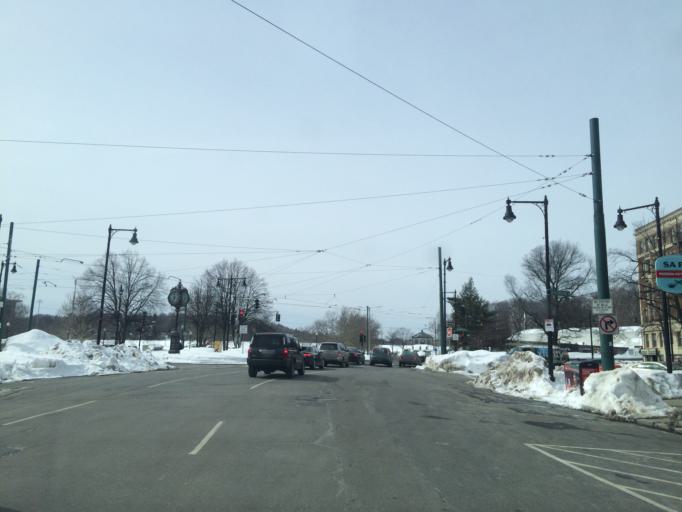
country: US
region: Massachusetts
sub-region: Norfolk County
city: Brookline
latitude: 42.3362
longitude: -71.1499
